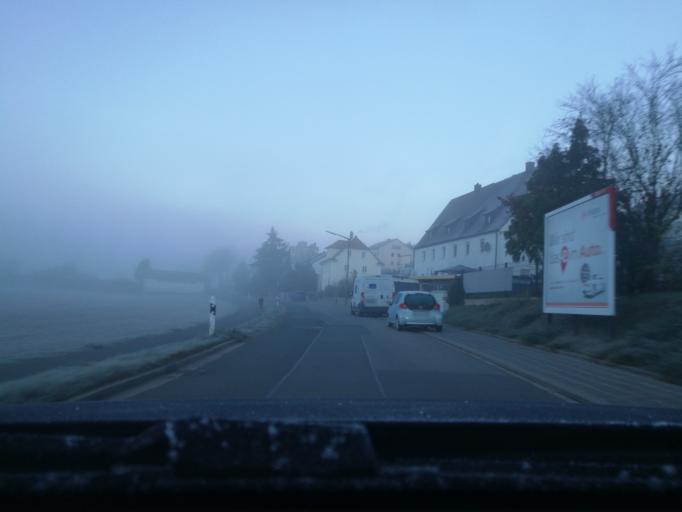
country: DE
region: Bavaria
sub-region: Regierungsbezirk Mittelfranken
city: Veitsbronn
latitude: 49.5112
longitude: 10.8790
